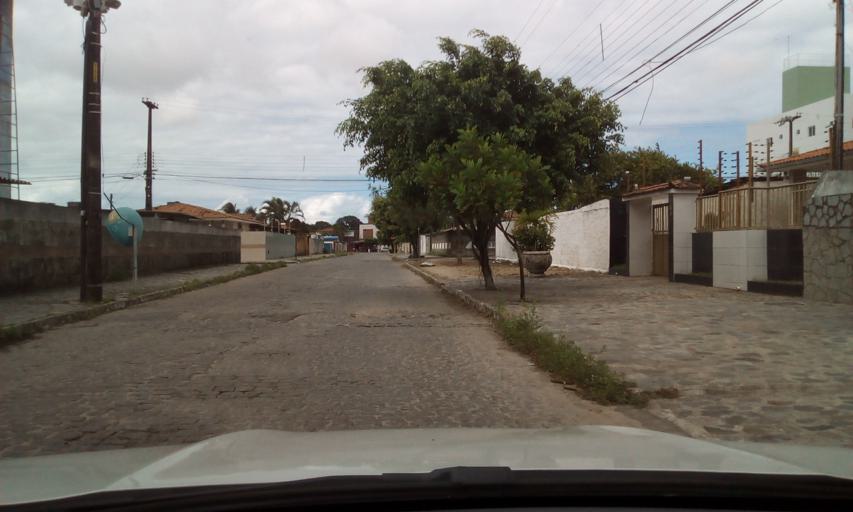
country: BR
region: Paraiba
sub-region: Joao Pessoa
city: Joao Pessoa
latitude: -7.1587
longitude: -34.8708
